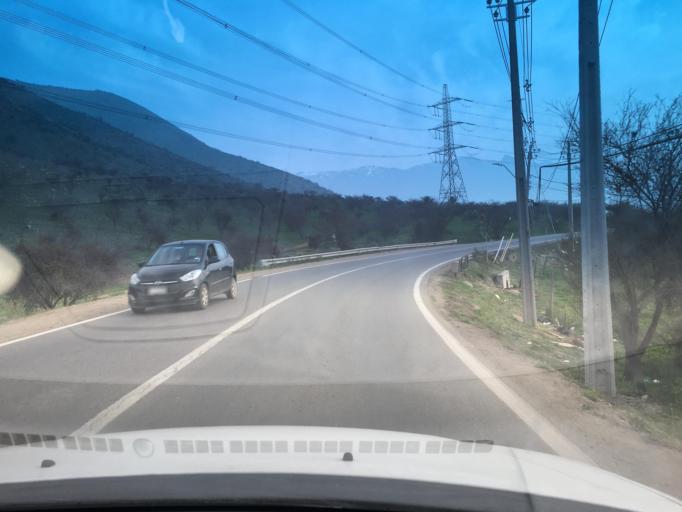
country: CL
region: Santiago Metropolitan
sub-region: Provincia de Chacabuco
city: Lampa
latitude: -33.2674
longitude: -70.8962
